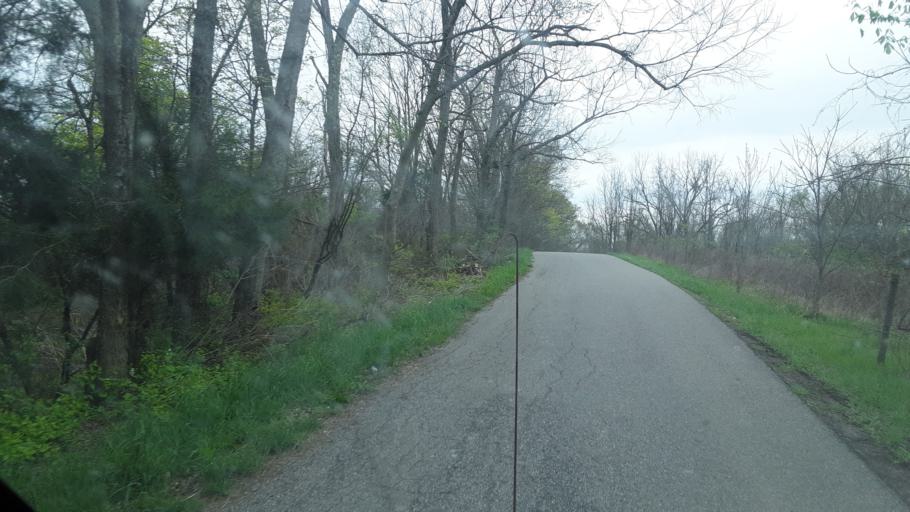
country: US
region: Kentucky
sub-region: Owen County
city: Owenton
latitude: 38.6635
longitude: -84.7717
